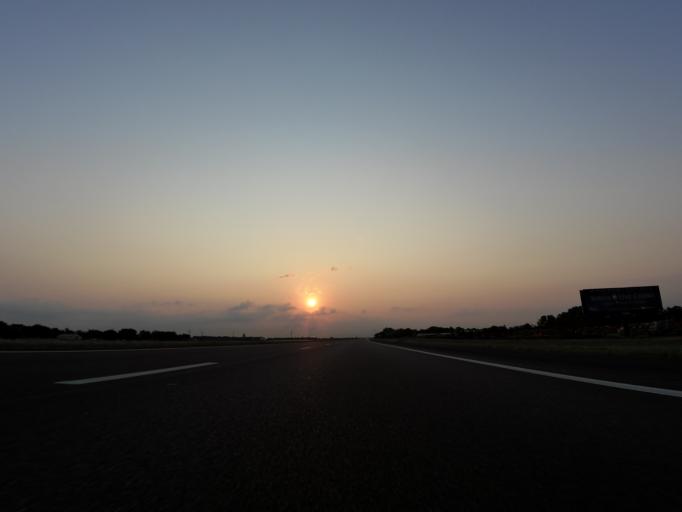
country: US
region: Kansas
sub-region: Reno County
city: Haven
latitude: 37.8763
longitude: -97.6701
